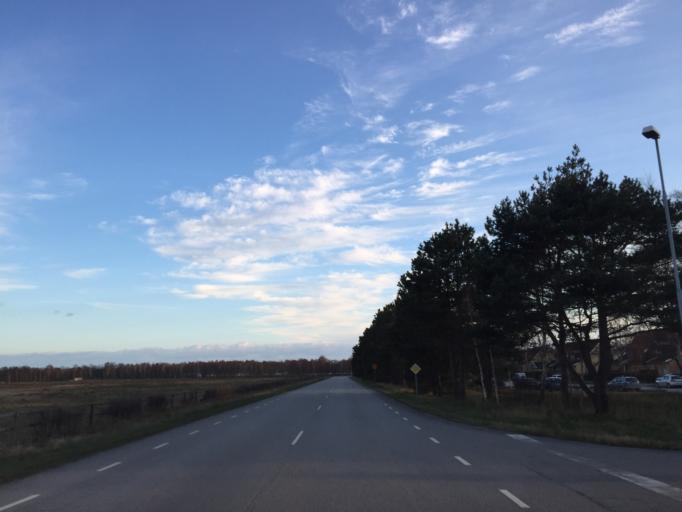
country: SE
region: Skane
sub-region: Vellinge Kommun
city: Skanor med Falsterbo
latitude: 55.4038
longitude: 12.8654
